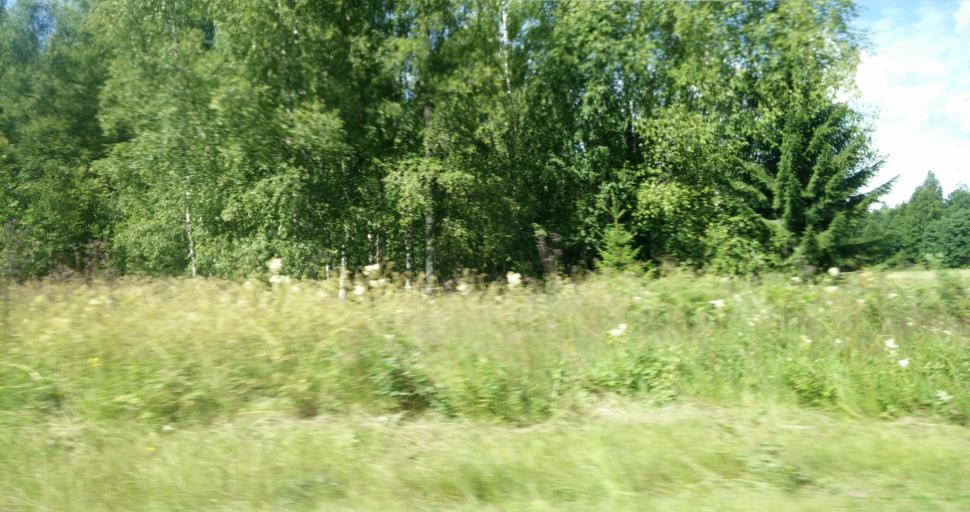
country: SE
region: Vaermland
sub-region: Hagfors Kommun
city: Ekshaerad
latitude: 60.1000
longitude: 13.4497
